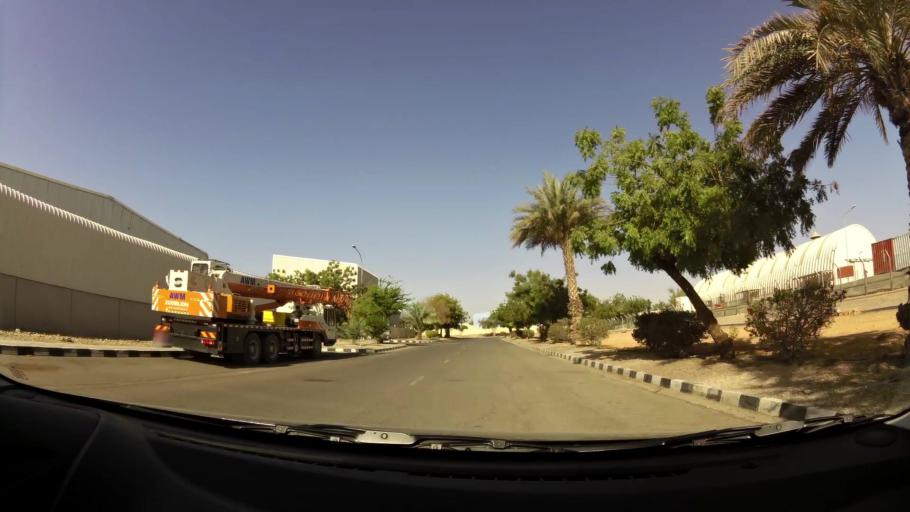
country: OM
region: Muhafazat Masqat
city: As Sib al Jadidah
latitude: 23.5553
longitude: 58.2006
